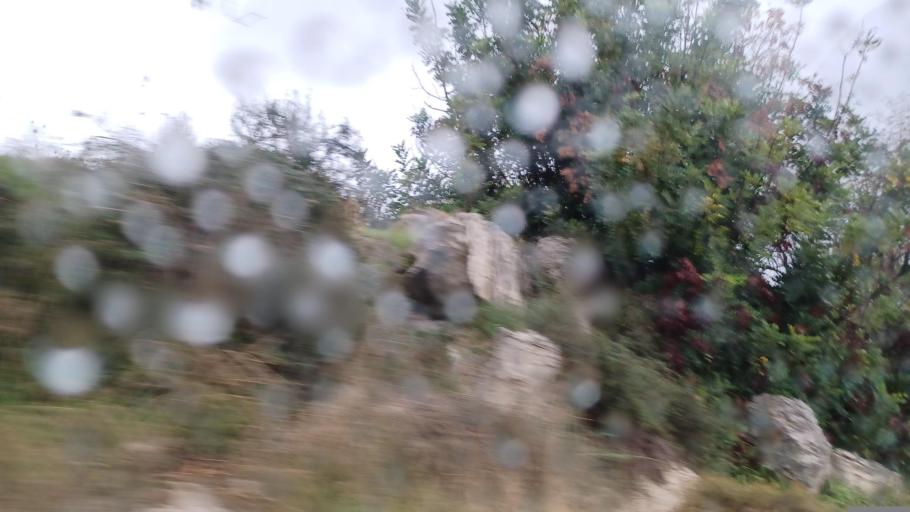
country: CY
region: Pafos
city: Mesogi
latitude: 34.8685
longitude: 32.5431
